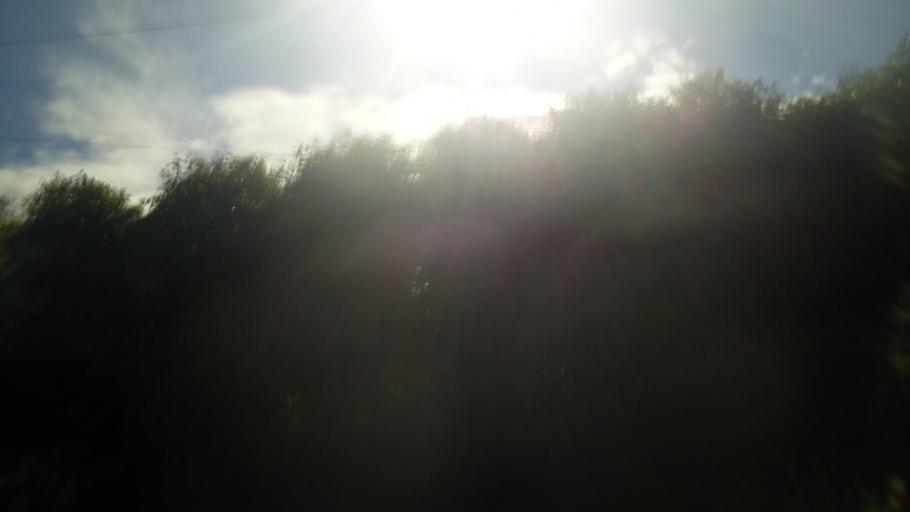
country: AU
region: Queensland
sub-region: Cassowary Coast
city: Innisfail
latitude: -17.5274
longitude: 145.9812
